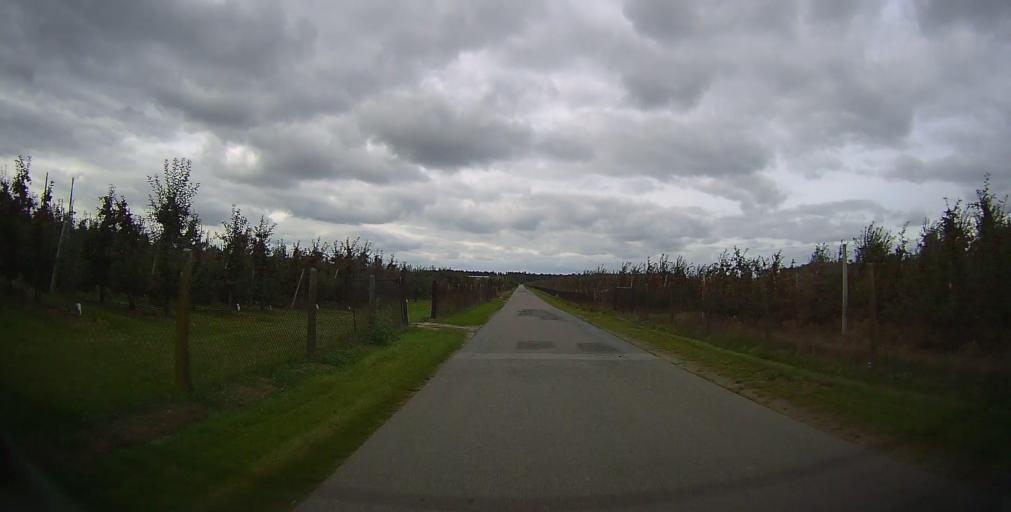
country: PL
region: Masovian Voivodeship
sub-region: Powiat grojecki
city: Goszczyn
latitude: 51.7658
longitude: 20.8683
